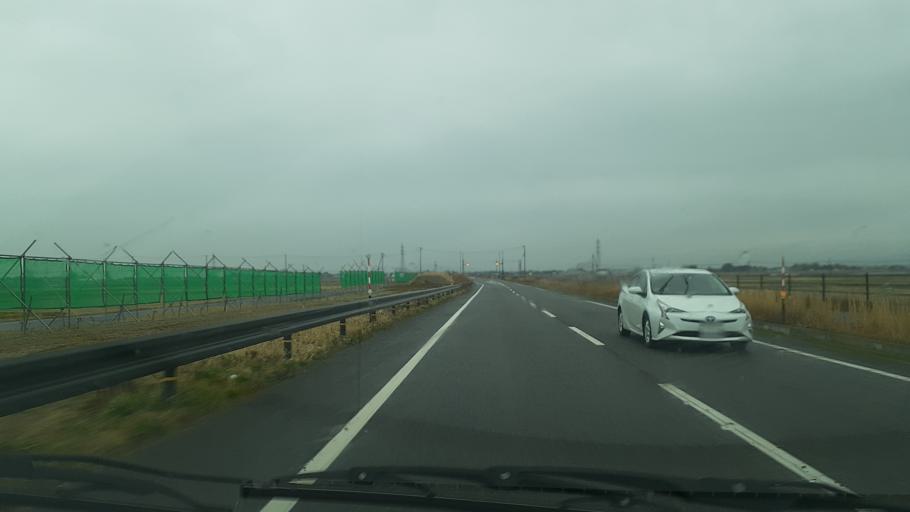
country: JP
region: Niigata
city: Kameda-honcho
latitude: 37.8675
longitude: 139.1424
